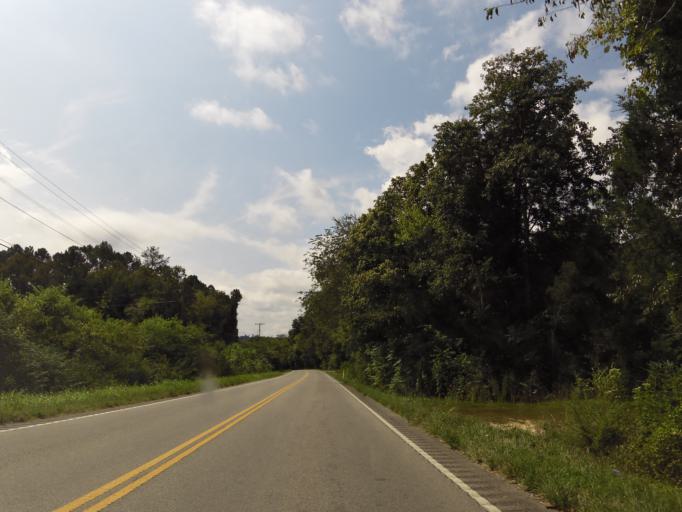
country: US
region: Tennessee
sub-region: Perry County
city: Linden
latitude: 35.6951
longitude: -87.8033
